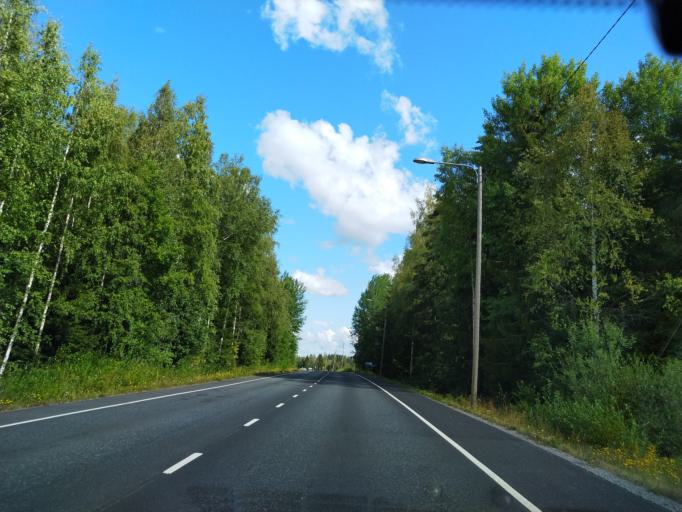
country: FI
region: Satakunta
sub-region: Pori
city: Huittinen
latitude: 61.1756
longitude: 22.7115
